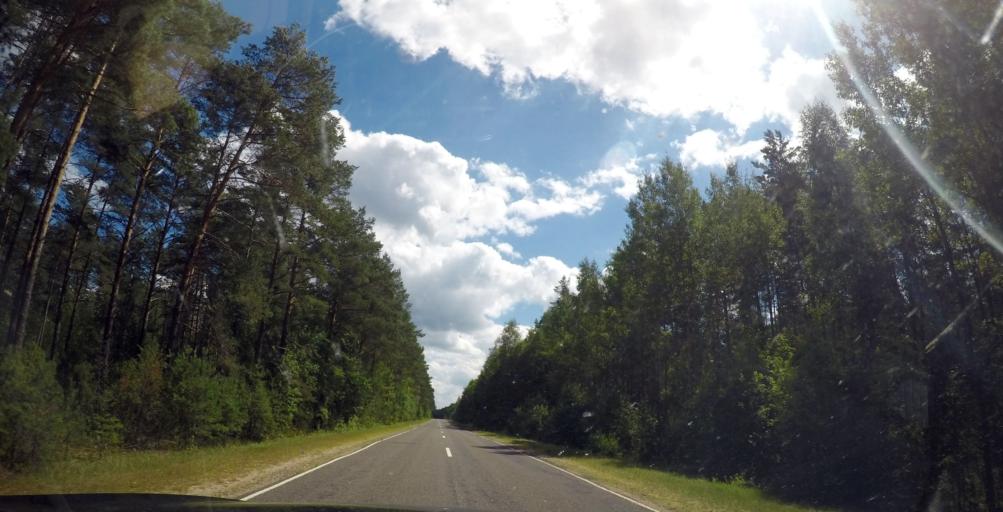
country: LT
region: Alytaus apskritis
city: Druskininkai
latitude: 53.8562
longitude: 24.1860
